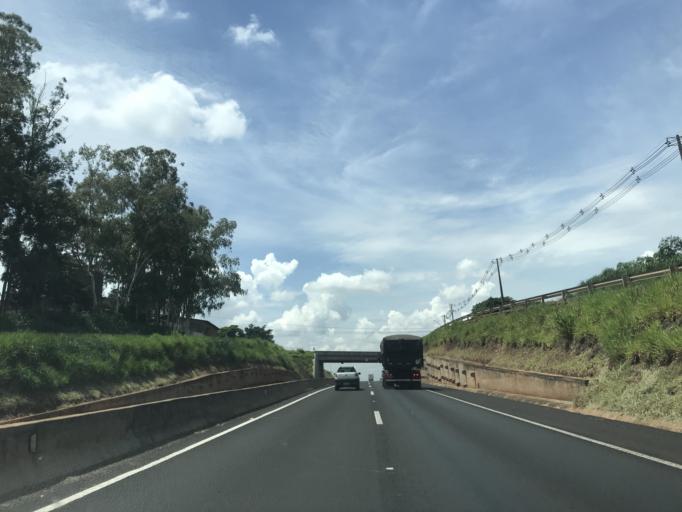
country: BR
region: Parana
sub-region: Alto Parana
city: Alto Parana
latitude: -23.1941
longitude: -52.2038
